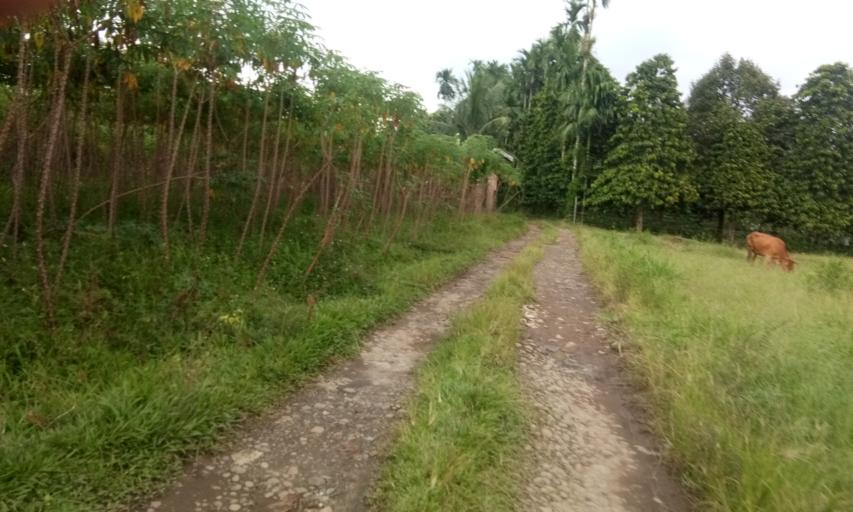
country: ID
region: North Sumatra
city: Deli Tua
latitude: 3.4666
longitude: 98.6108
